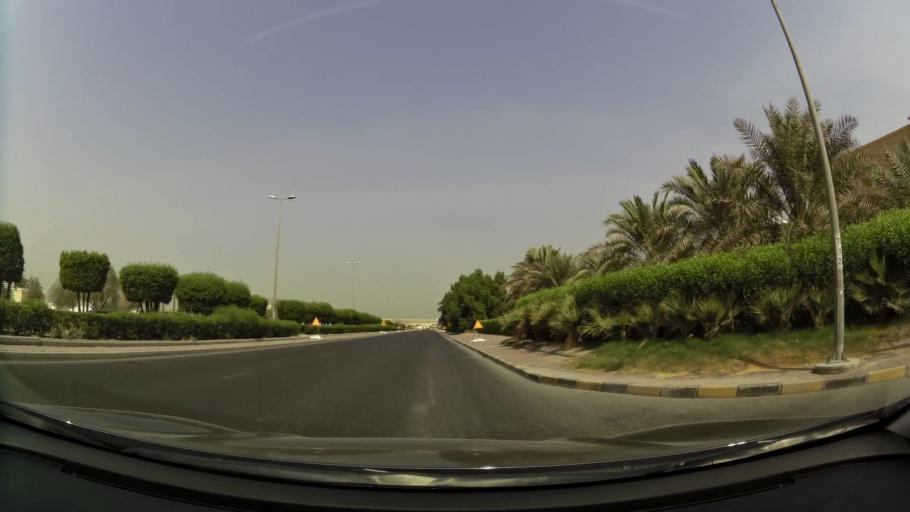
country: KW
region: Al Asimah
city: Ar Rabiyah
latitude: 29.3055
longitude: 47.8654
